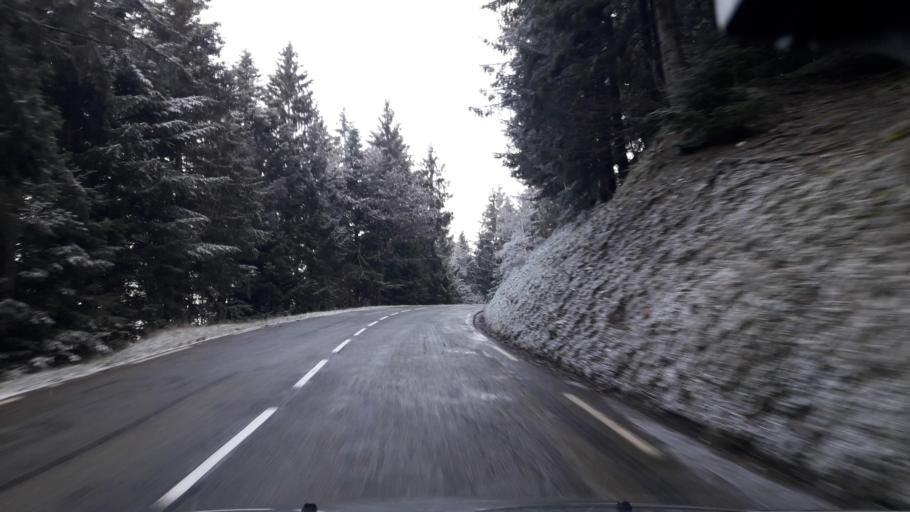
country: FR
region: Rhone-Alpes
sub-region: Departement de l'Isere
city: Allevard
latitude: 45.3946
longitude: 6.0901
